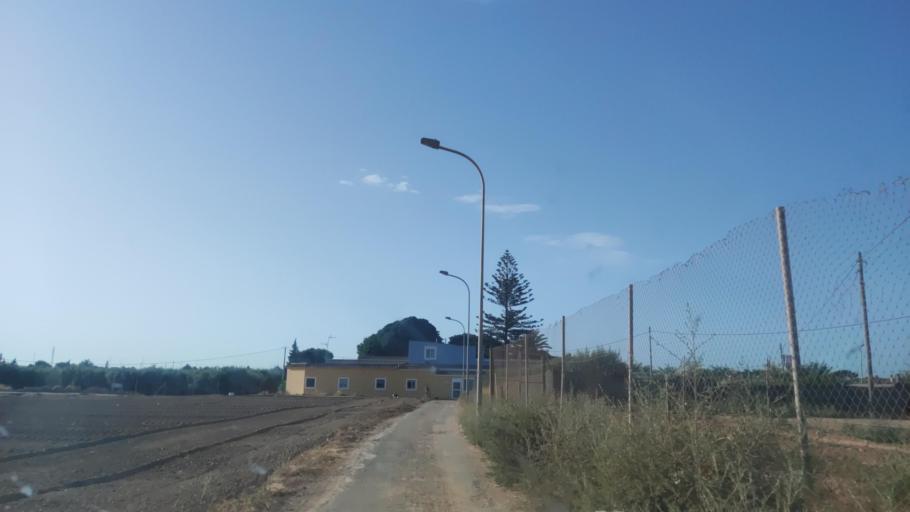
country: ES
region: Murcia
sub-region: Murcia
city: San Javier
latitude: 37.8094
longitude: -0.8553
